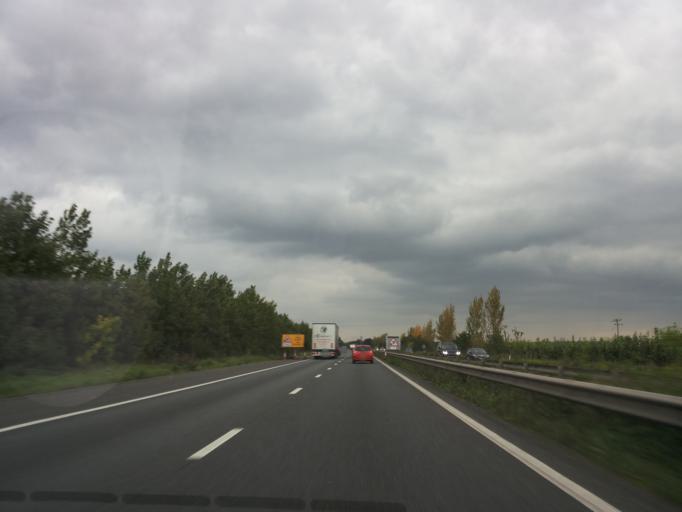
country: GB
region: England
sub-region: Kent
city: Sittingbourne
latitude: 51.3138
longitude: 0.7037
